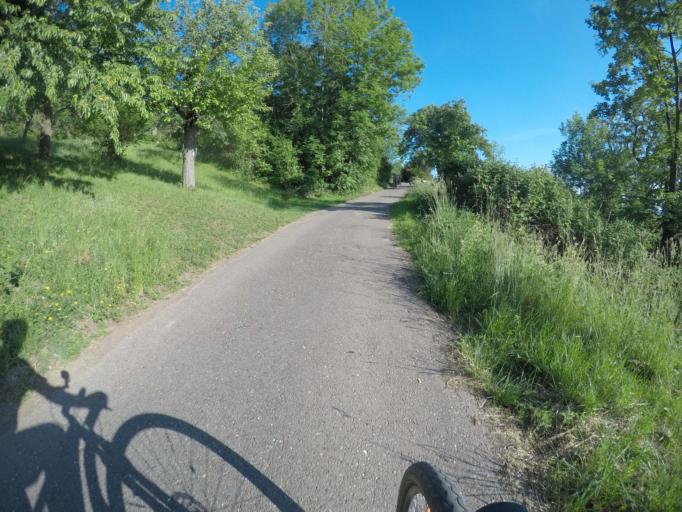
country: DE
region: Baden-Wuerttemberg
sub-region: Regierungsbezirk Stuttgart
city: Esslingen
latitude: 48.7603
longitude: 9.3218
